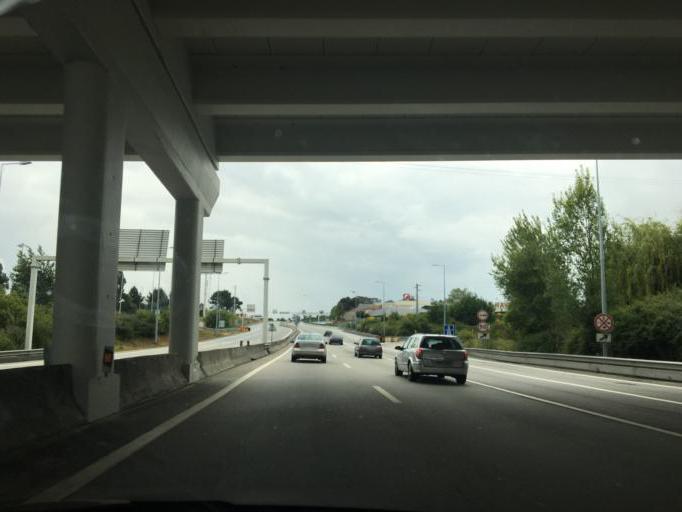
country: PT
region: Porto
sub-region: Maia
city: Leca do Bailio
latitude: 41.2030
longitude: -8.6275
